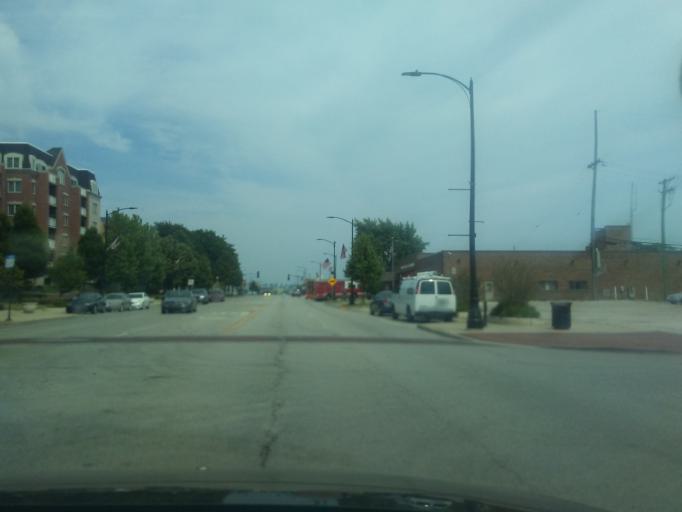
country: US
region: Illinois
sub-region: Cook County
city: Harwood Heights
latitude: 41.9670
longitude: -87.8146
